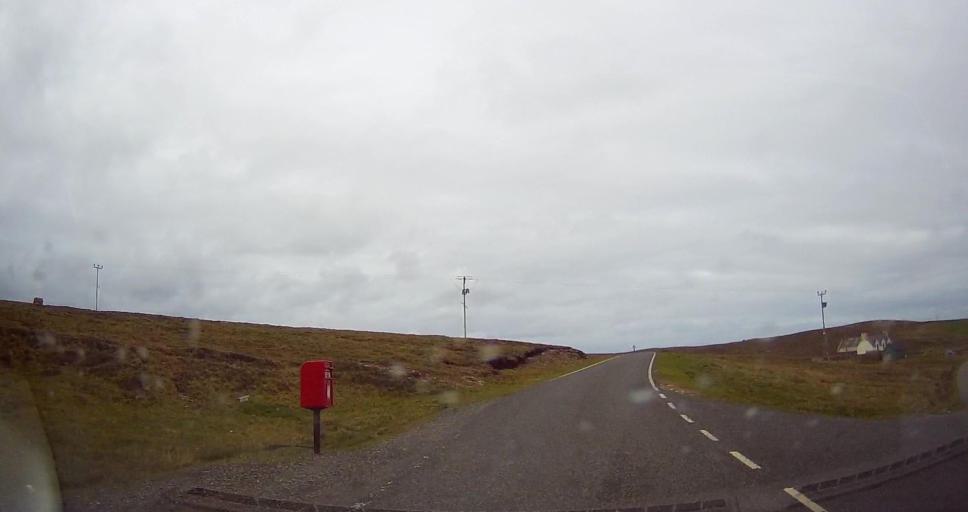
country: GB
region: Scotland
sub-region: Shetland Islands
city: Lerwick
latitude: 60.4942
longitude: -1.5655
